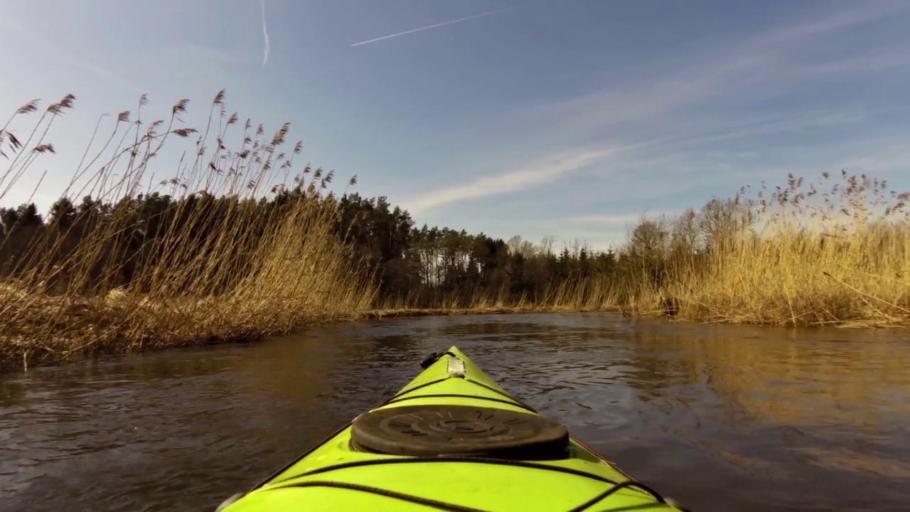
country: PL
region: West Pomeranian Voivodeship
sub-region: Powiat lobeski
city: Lobez
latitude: 53.6498
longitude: 15.5700
